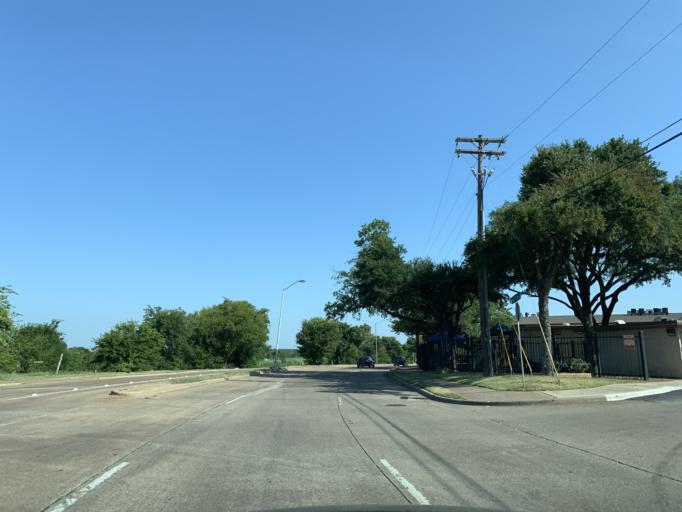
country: US
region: Texas
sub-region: Dallas County
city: Hutchins
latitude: 32.6740
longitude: -96.7636
